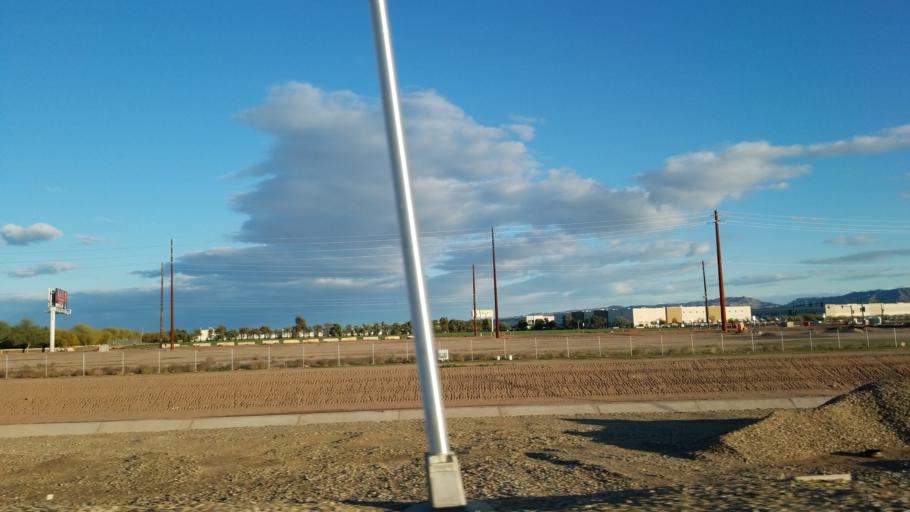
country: US
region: Arizona
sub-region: Maricopa County
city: Laveen
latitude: 33.4243
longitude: -112.1883
